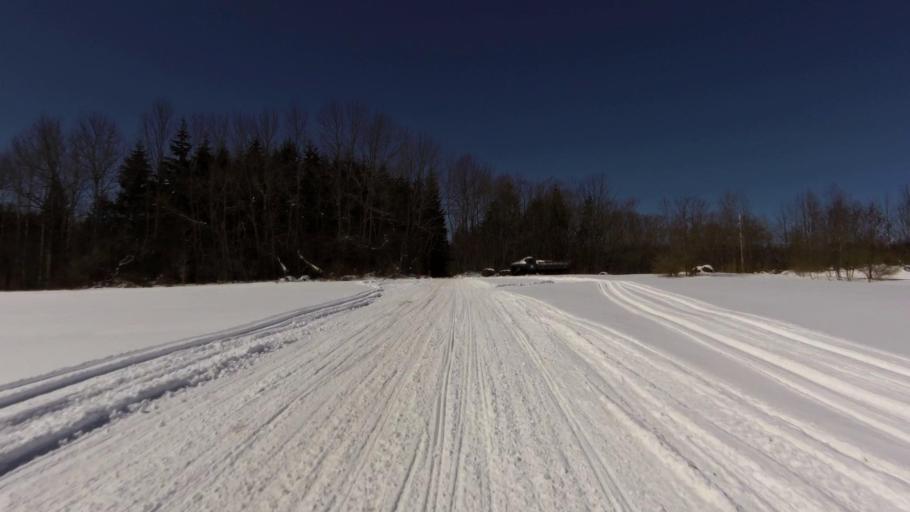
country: US
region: New York
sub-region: Allegany County
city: Houghton
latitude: 42.4089
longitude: -78.2859
